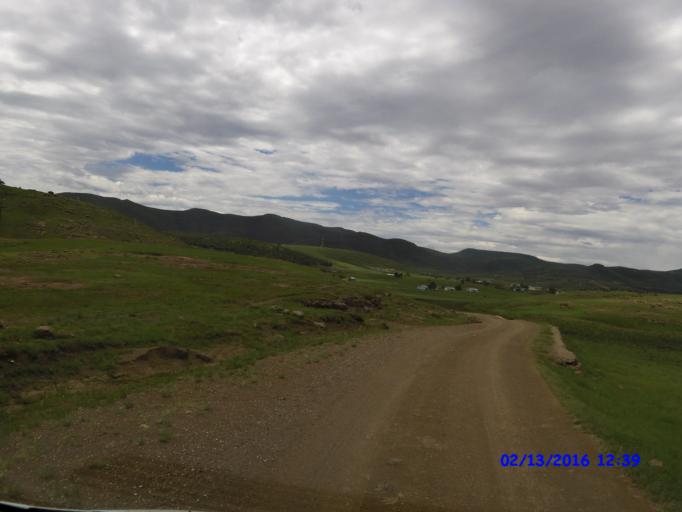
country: LS
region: Maseru
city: Nako
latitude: -29.8332
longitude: 28.0301
